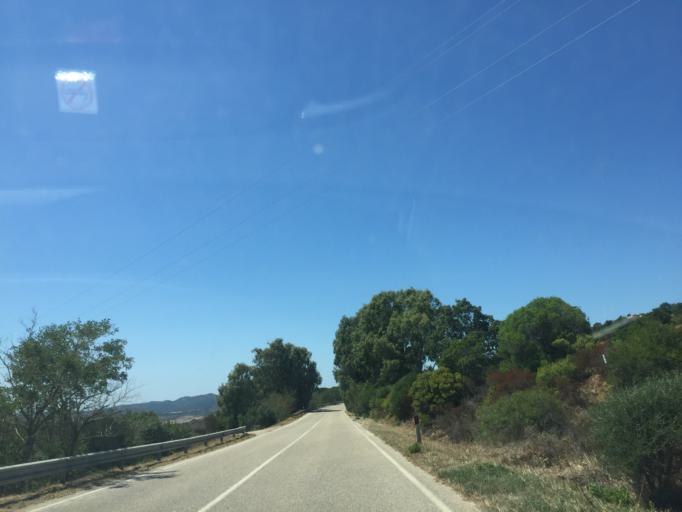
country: IT
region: Sardinia
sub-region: Provincia di Olbia-Tempio
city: Aglientu
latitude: 41.0982
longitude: 9.0874
